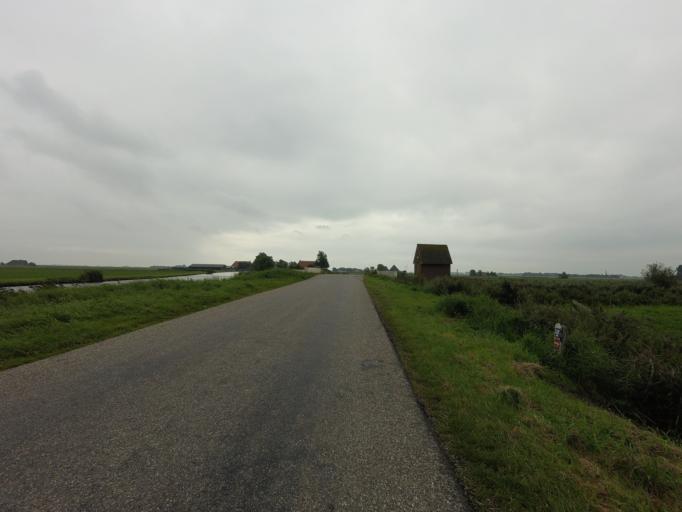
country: NL
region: Friesland
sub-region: Sudwest Fryslan
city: Workum
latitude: 53.0019
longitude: 5.4726
